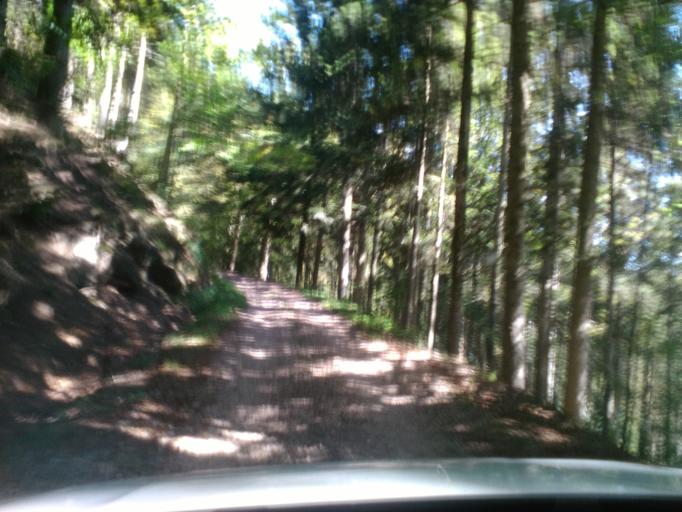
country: FR
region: Lorraine
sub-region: Departement des Vosges
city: Senones
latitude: 48.4199
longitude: 6.9836
